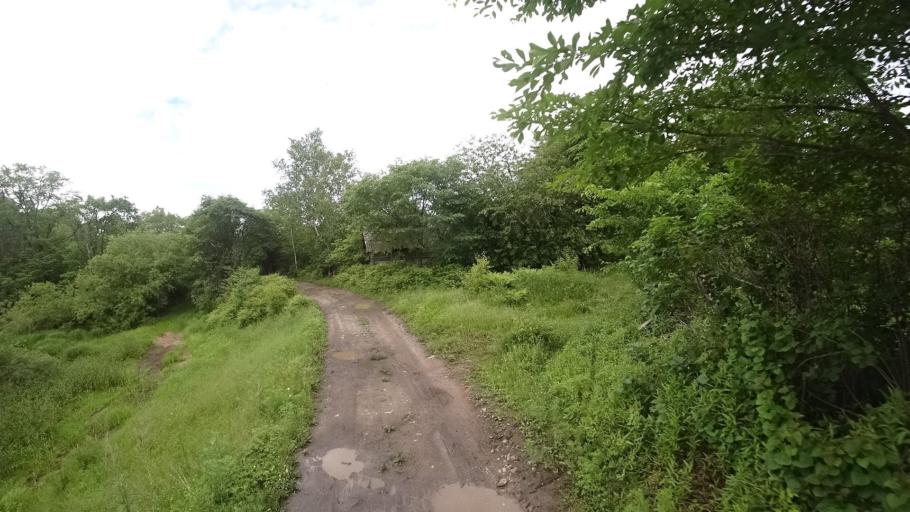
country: RU
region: Khabarovsk Krai
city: Amursk
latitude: 49.9058
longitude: 136.1324
